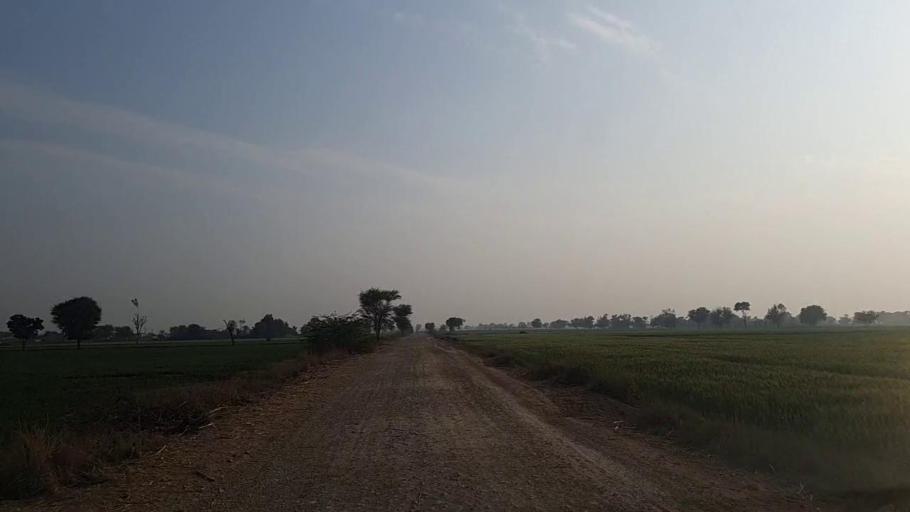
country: PK
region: Sindh
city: Jam Sahib
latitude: 26.3145
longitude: 68.5336
